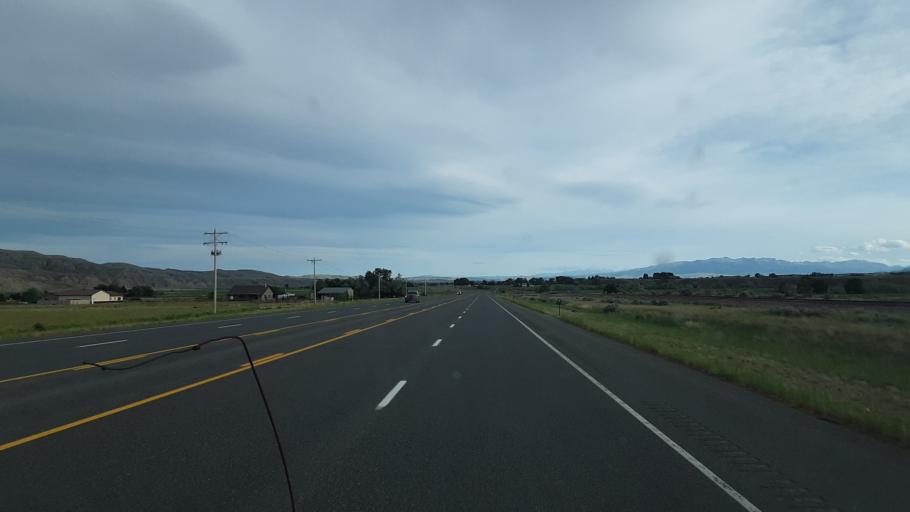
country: US
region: Wyoming
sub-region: Park County
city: Cody
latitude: 44.6436
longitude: -108.9533
